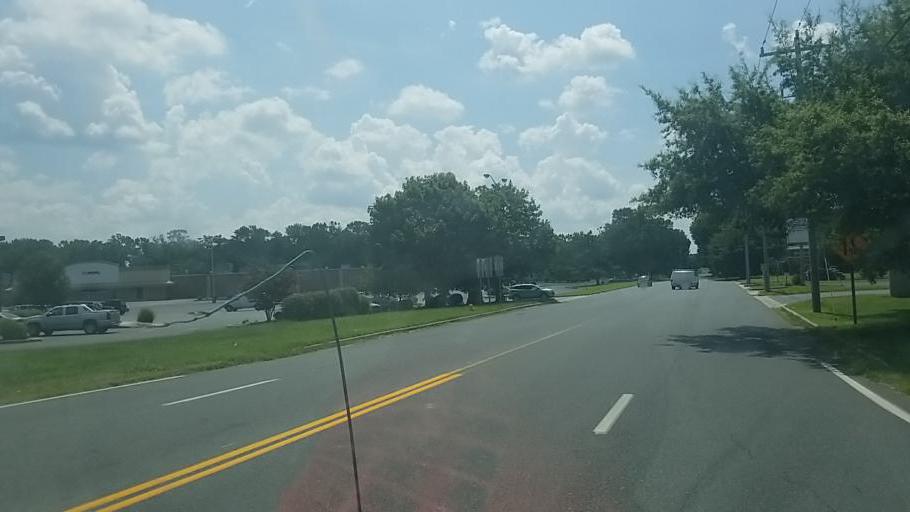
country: US
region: Maryland
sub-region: Wicomico County
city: Salisbury
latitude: 38.3652
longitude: -75.5479
